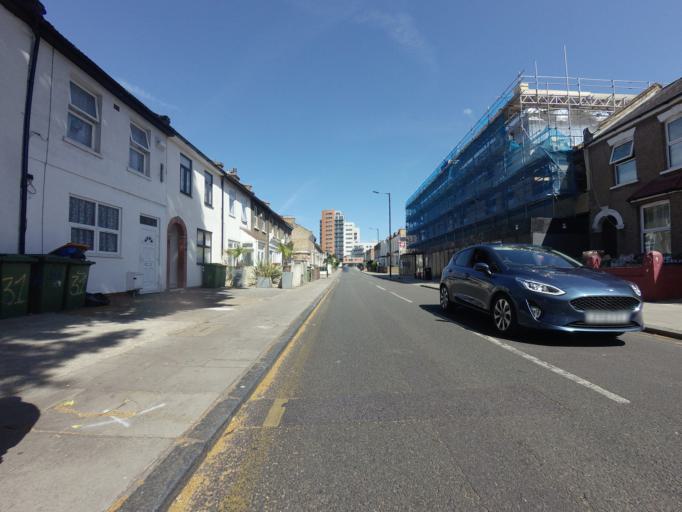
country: GB
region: England
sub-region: Greater London
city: Poplar
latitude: 51.5450
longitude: 0.0080
